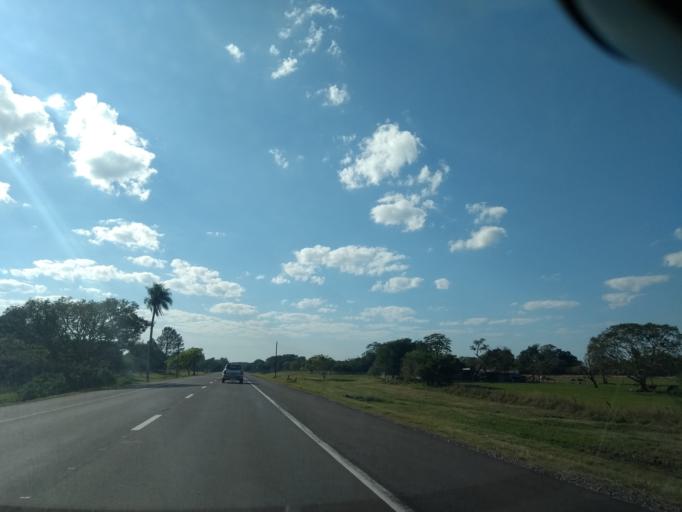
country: AR
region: Corrientes
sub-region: Departamento de San Cosme
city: San Cosme
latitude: -27.3672
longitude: -58.4661
